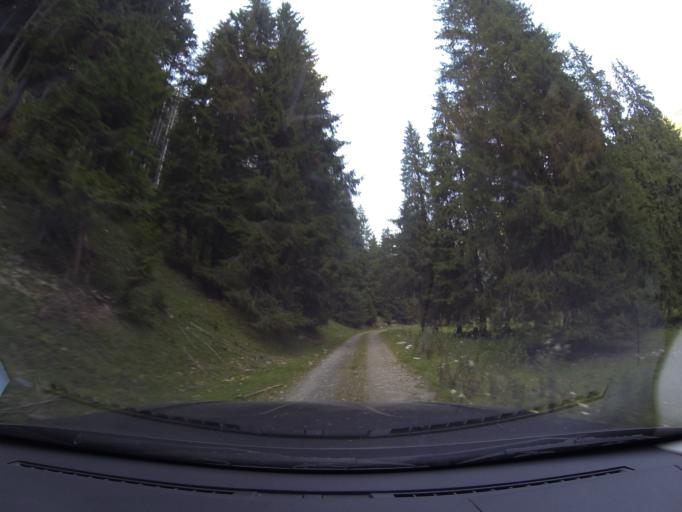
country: RO
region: Brasov
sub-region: Oras Victoria
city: Victoria
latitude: 45.5674
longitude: 24.6940
